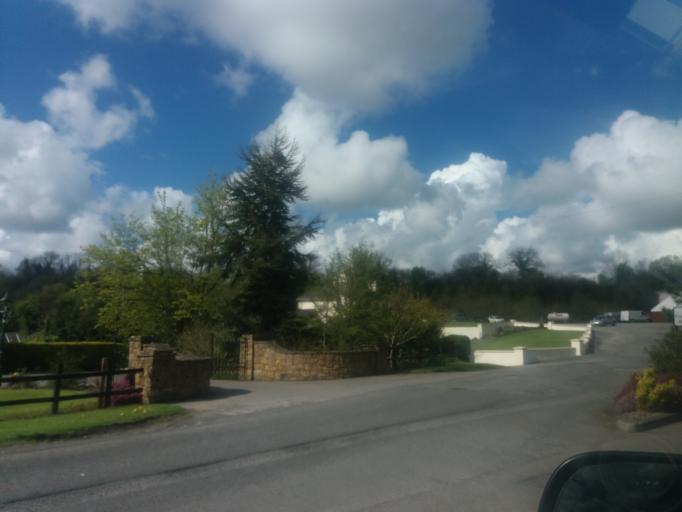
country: IE
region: Ulster
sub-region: An Cabhan
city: Cavan
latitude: 53.9835
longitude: -7.3446
